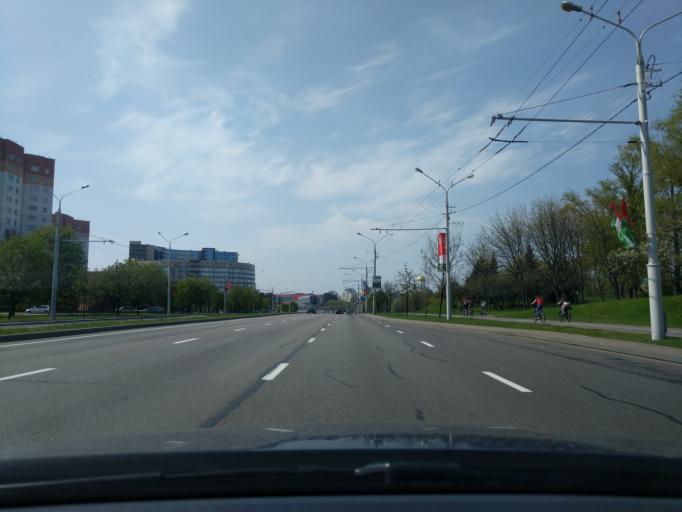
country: BY
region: Minsk
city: Novoye Medvezhino
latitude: 53.9346
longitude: 27.5012
